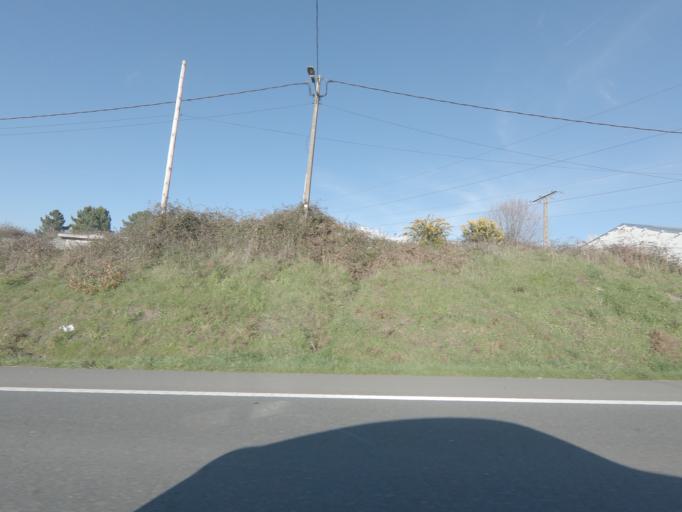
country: ES
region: Galicia
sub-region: Provincia de Pontevedra
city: Silleda
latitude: 42.7125
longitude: -8.2785
